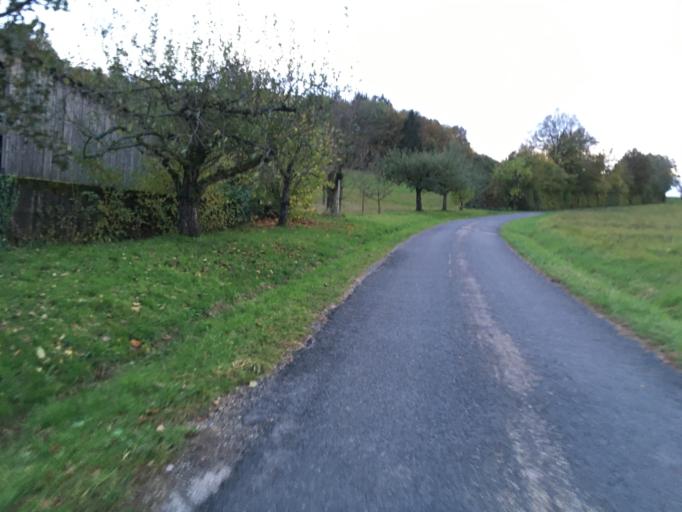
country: DE
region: Baden-Wuerttemberg
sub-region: Karlsruhe Region
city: Rosenberg
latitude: 49.3915
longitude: 9.4752
